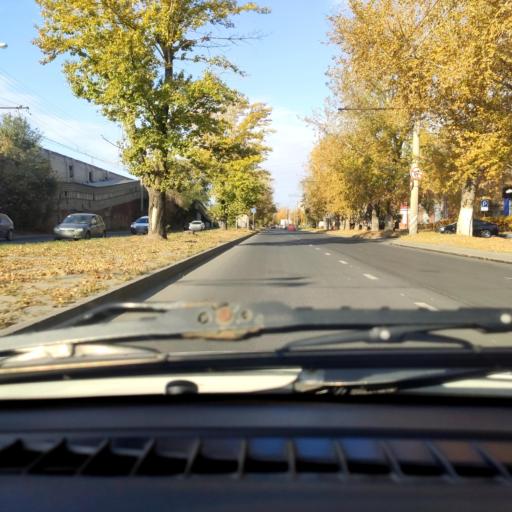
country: RU
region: Samara
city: Tol'yatti
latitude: 53.5161
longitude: 49.4353
